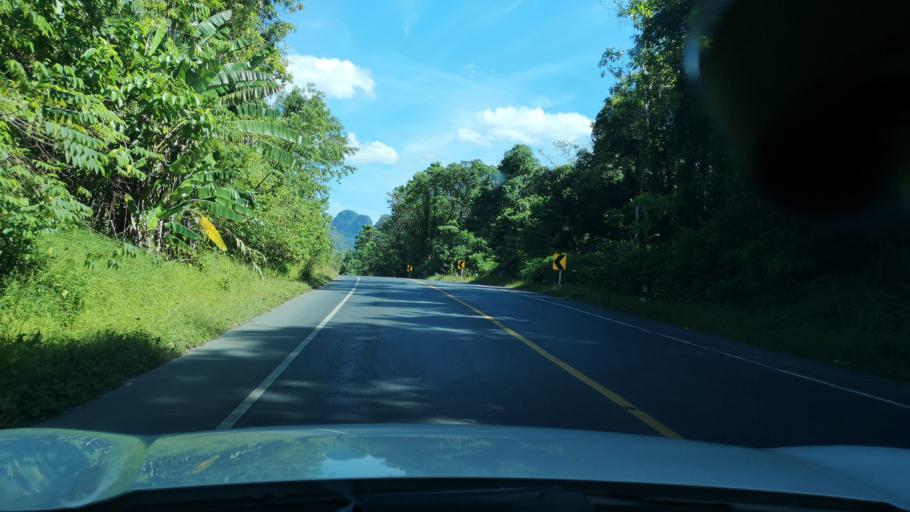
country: TH
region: Phangnga
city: Phang Nga
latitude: 8.5333
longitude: 98.5064
